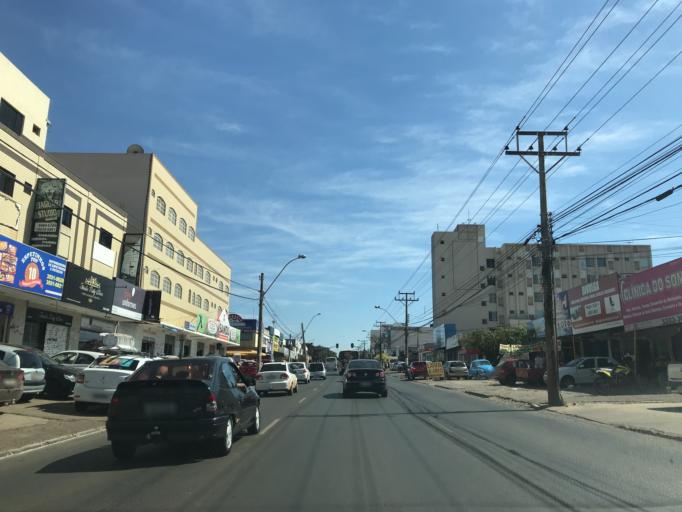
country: BR
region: Federal District
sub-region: Brasilia
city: Brasilia
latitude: -15.8157
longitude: -48.0668
